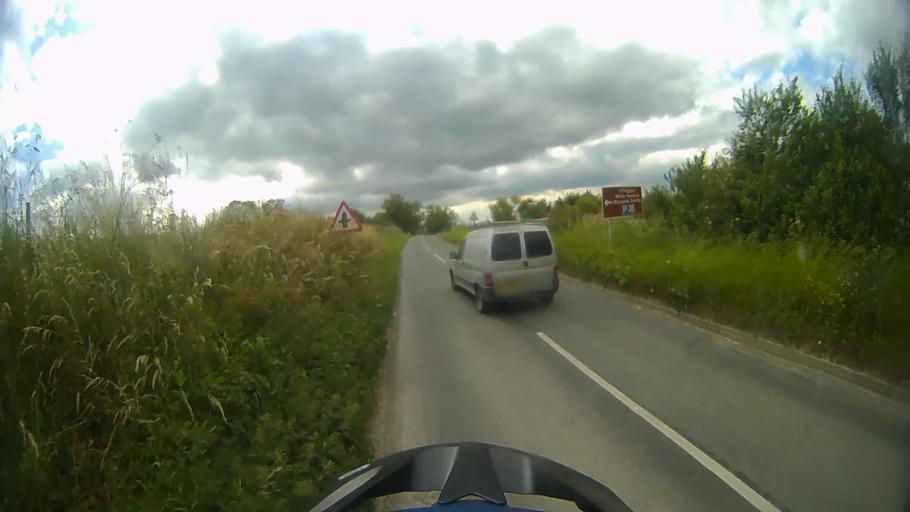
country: GB
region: England
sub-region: Oxfordshire
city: Faringdon
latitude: 51.5828
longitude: -1.5756
